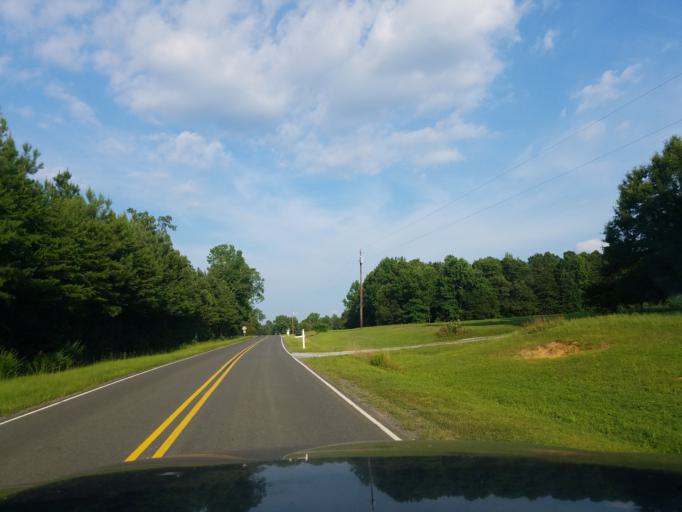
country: US
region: North Carolina
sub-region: Granville County
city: Butner
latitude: 36.1951
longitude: -78.8360
